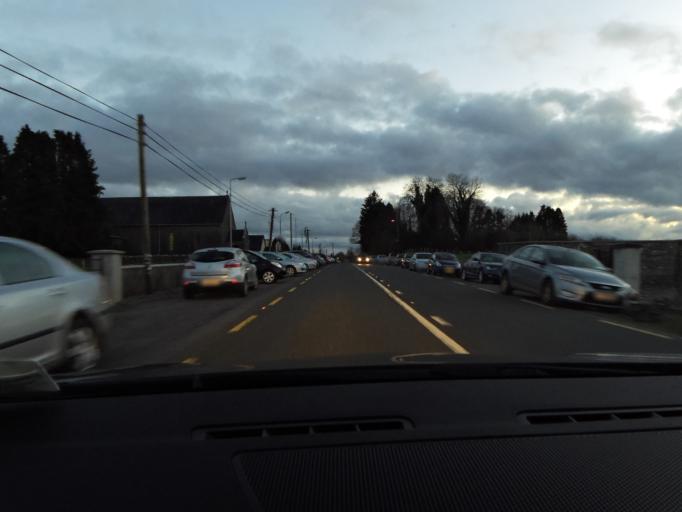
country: IE
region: Connaught
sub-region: Roscommon
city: Boyle
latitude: 53.8067
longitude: -8.2301
